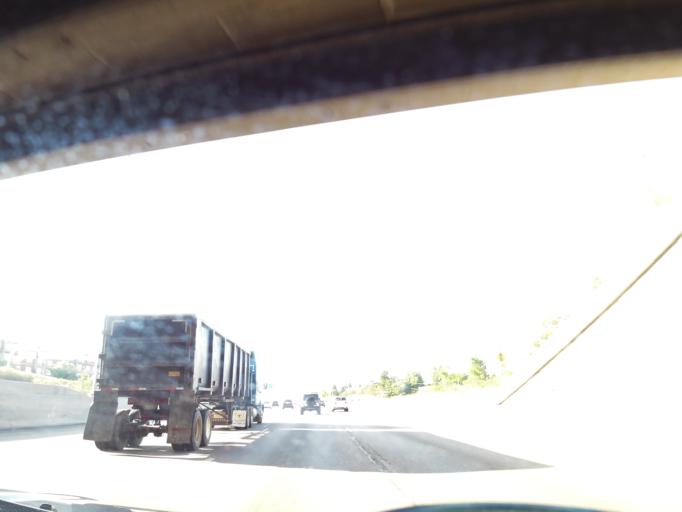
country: US
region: Colorado
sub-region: Arapahoe County
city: Cherry Hills Village
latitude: 39.6530
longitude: -104.9185
